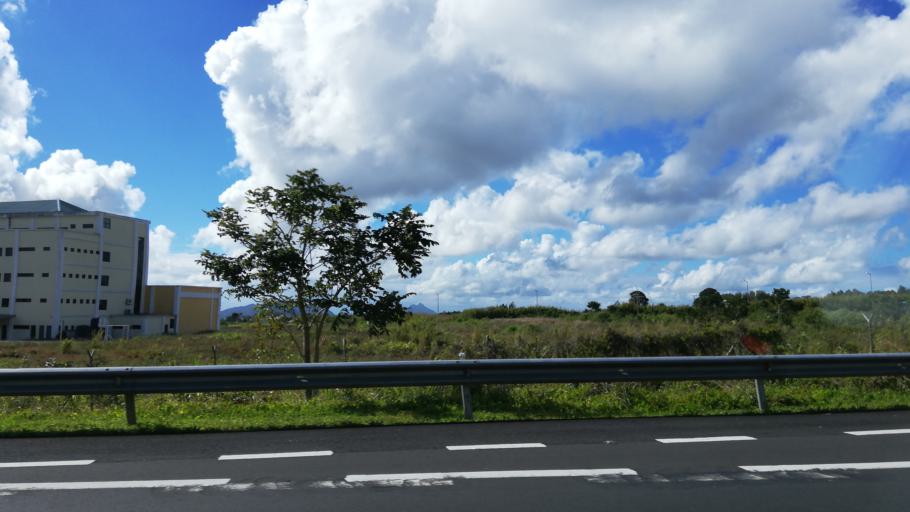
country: MU
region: Moka
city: Quartier Militaire
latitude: -20.2523
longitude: 57.5854
